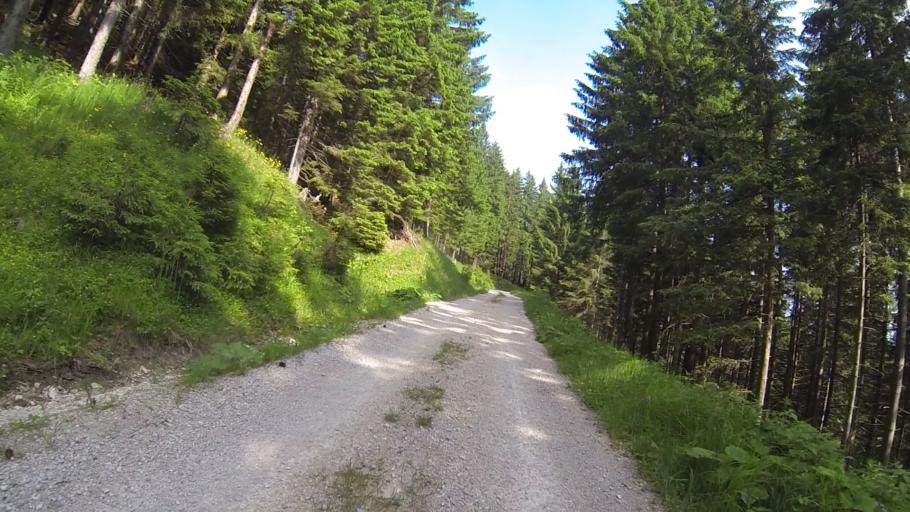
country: DE
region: Bavaria
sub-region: Swabia
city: Nesselwang
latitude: 47.5866
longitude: 10.4973
